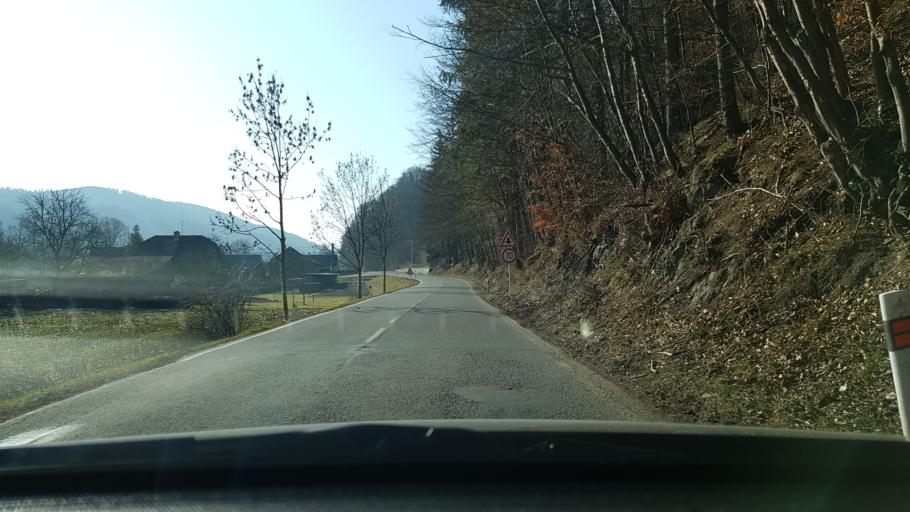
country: CZ
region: Olomoucky
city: Dolni Bohdikov
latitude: 50.0112
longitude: 16.8948
